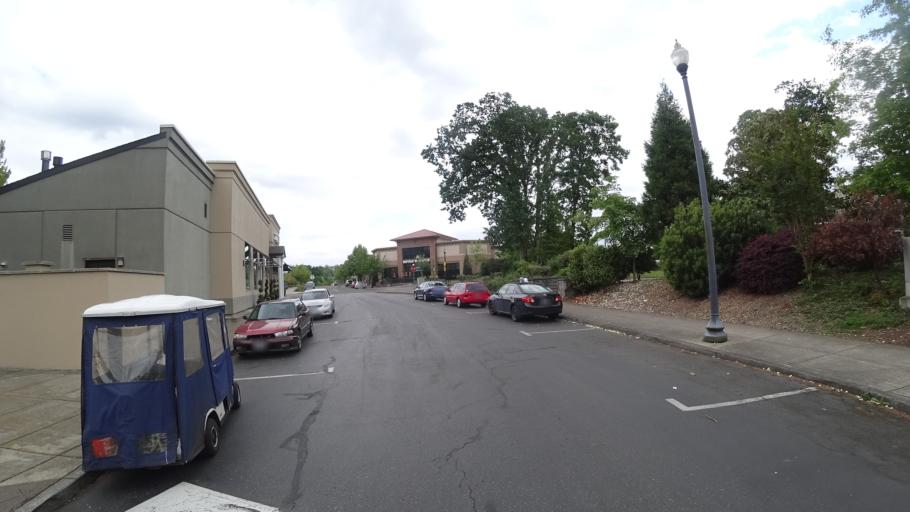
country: US
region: Oregon
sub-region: Washington County
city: Rockcreek
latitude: 45.5386
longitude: -122.8796
